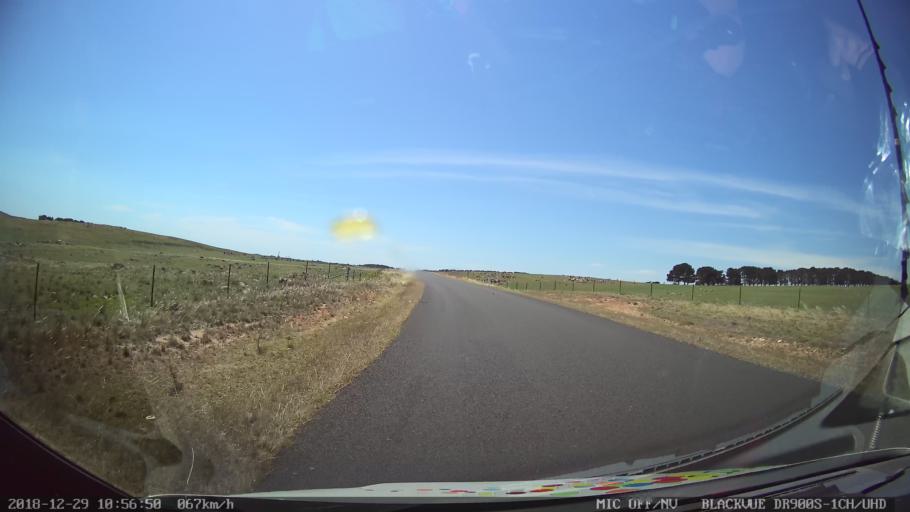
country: AU
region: New South Wales
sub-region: Palerang
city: Bungendore
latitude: -35.1381
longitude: 149.5407
